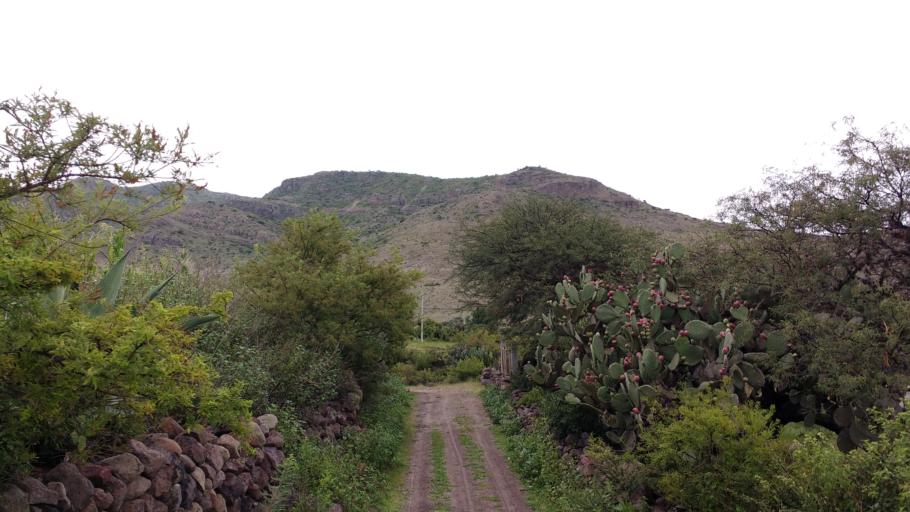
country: MX
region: Hidalgo
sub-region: Tezontepec de Aldama
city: Tenango
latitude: 20.2741
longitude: -99.2872
